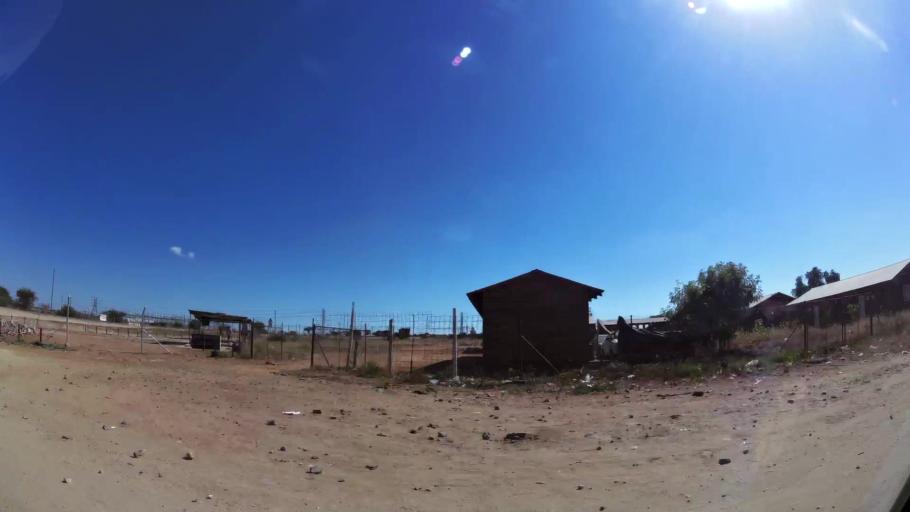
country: ZA
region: Limpopo
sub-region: Capricorn District Municipality
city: Polokwane
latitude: -23.8924
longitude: 29.4100
